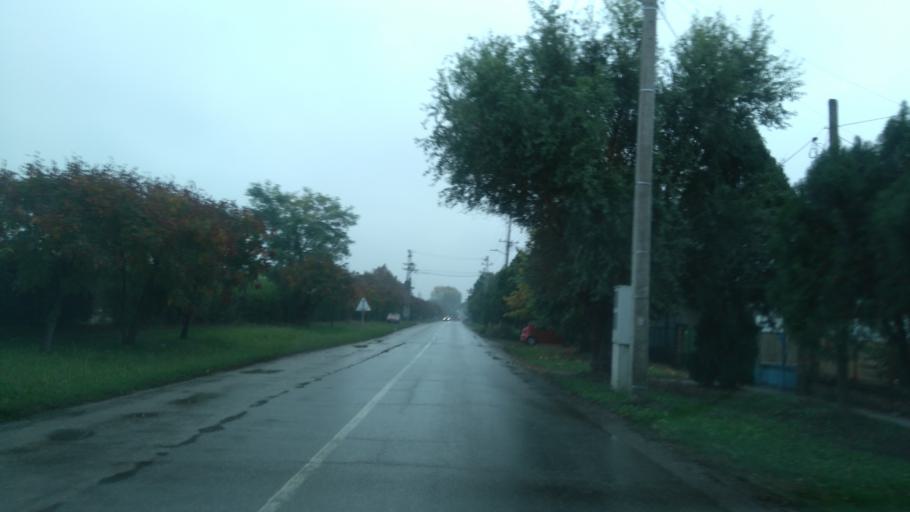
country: RS
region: Autonomna Pokrajina Vojvodina
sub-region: Juznobacki Okrug
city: Becej
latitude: 45.6163
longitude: 20.0315
